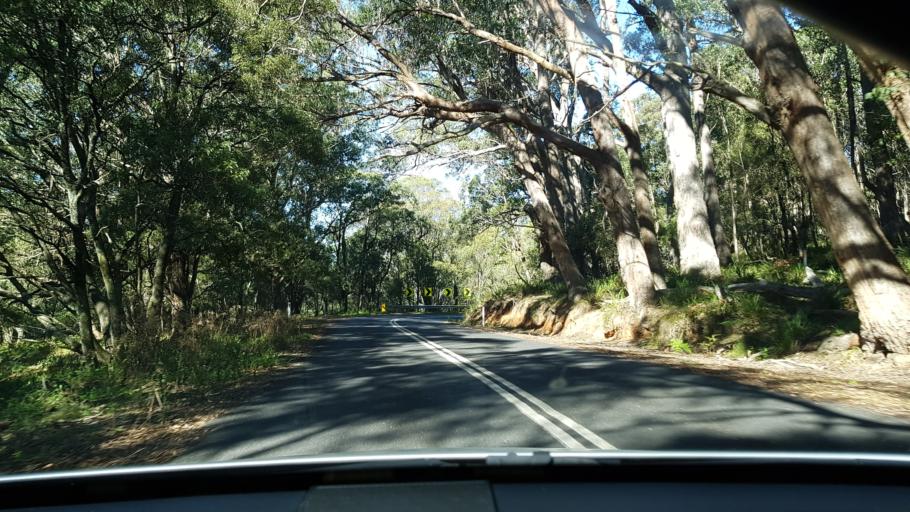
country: AU
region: New South Wales
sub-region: Oberon
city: Oberon
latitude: -33.7888
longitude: 150.0279
